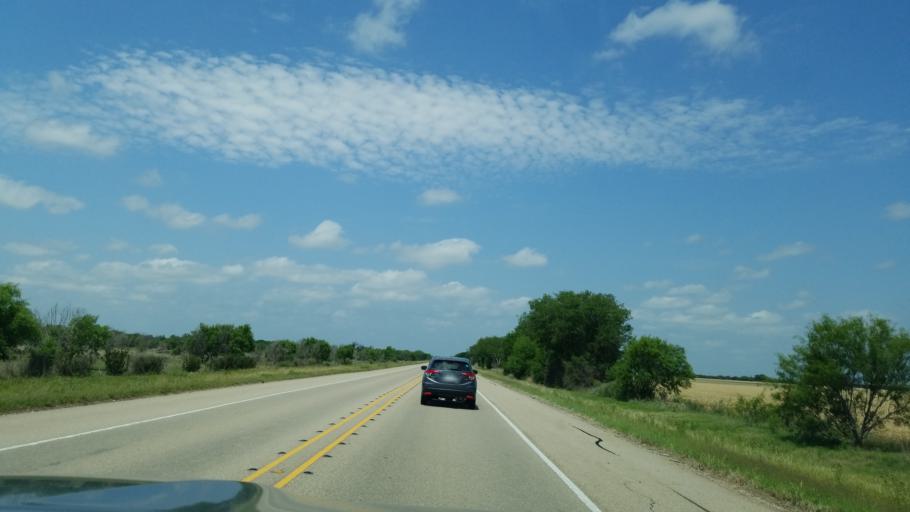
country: US
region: Texas
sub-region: Frio County
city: Pearsall
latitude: 29.0065
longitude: -99.1506
